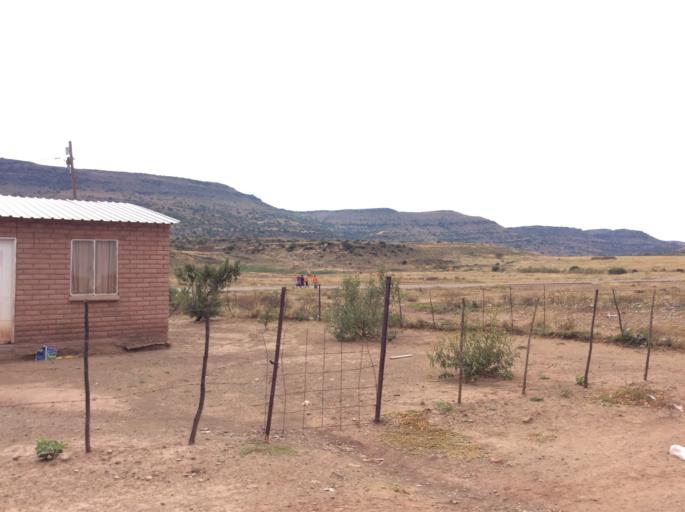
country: LS
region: Mafeteng
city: Mafeteng
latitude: -29.7183
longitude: 27.0206
